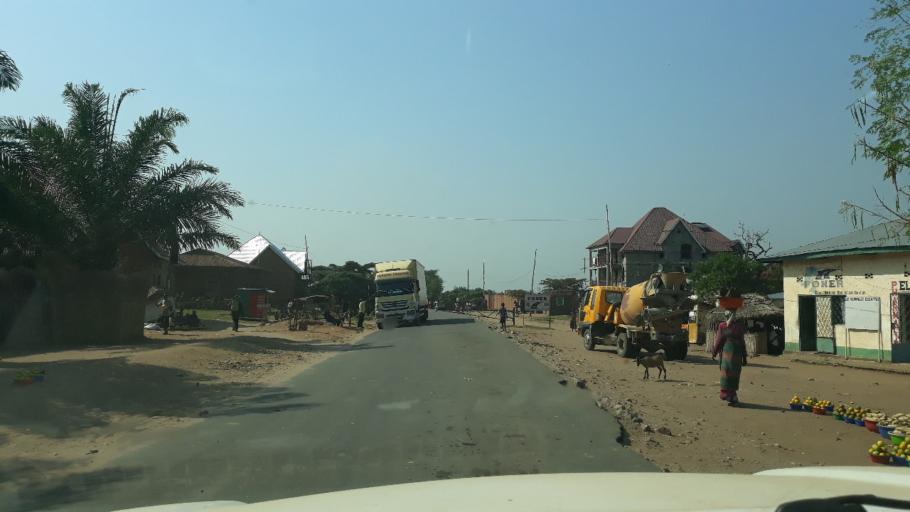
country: CD
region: South Kivu
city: Uvira
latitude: -3.2331
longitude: 29.1655
